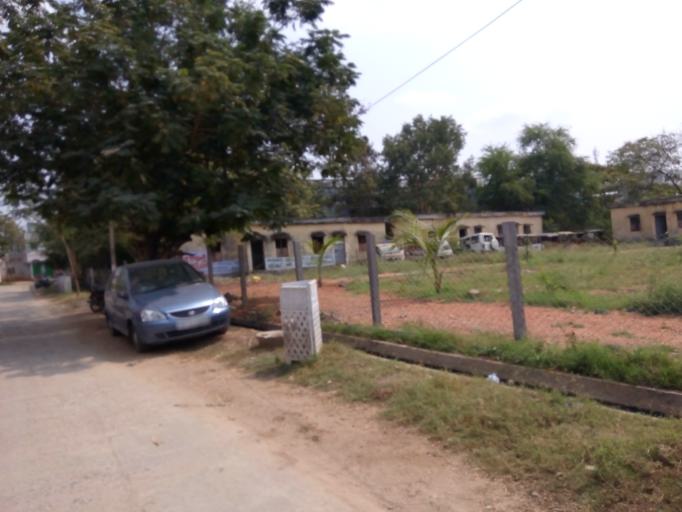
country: IN
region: Andhra Pradesh
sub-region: Prakasam
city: pedda nakkalapalem
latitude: 15.9691
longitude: 80.2756
